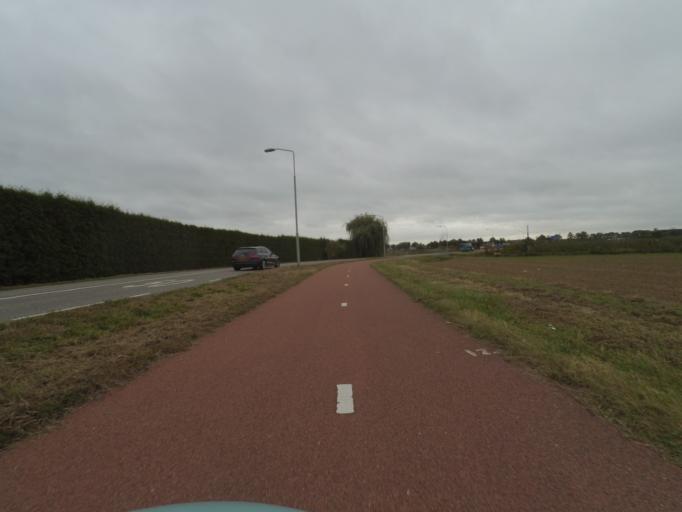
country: NL
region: Gelderland
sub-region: Gemeente Tiel
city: Tiel
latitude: 51.9045
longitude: 5.4215
